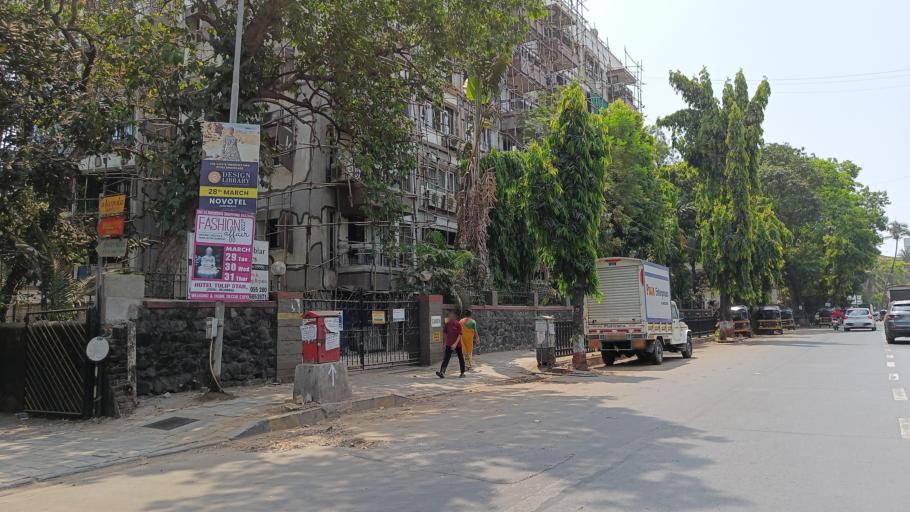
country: IN
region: Maharashtra
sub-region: Mumbai Suburban
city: Mumbai
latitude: 19.0944
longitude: 72.8283
